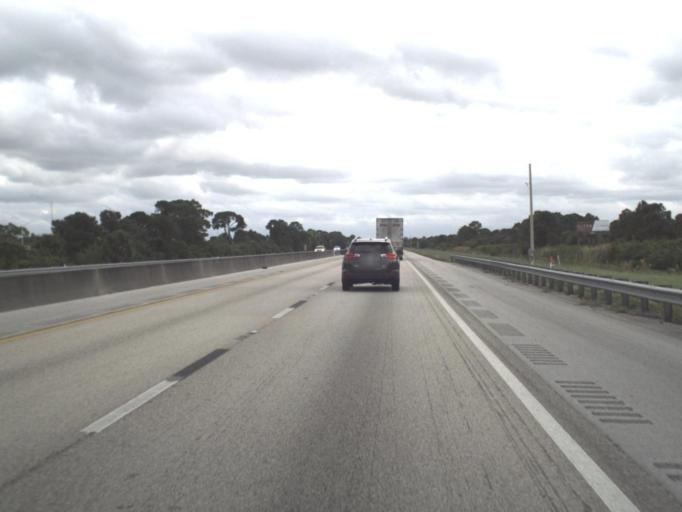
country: US
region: Florida
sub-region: Palm Beach County
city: Limestone Creek
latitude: 26.9099
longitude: -80.1430
